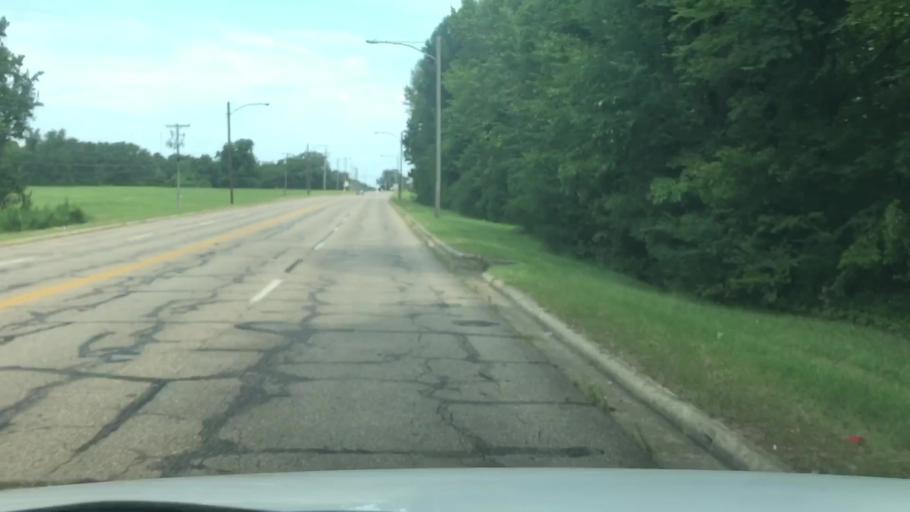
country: US
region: Texas
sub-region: Bowie County
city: Wake Village
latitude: 33.4107
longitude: -94.0803
